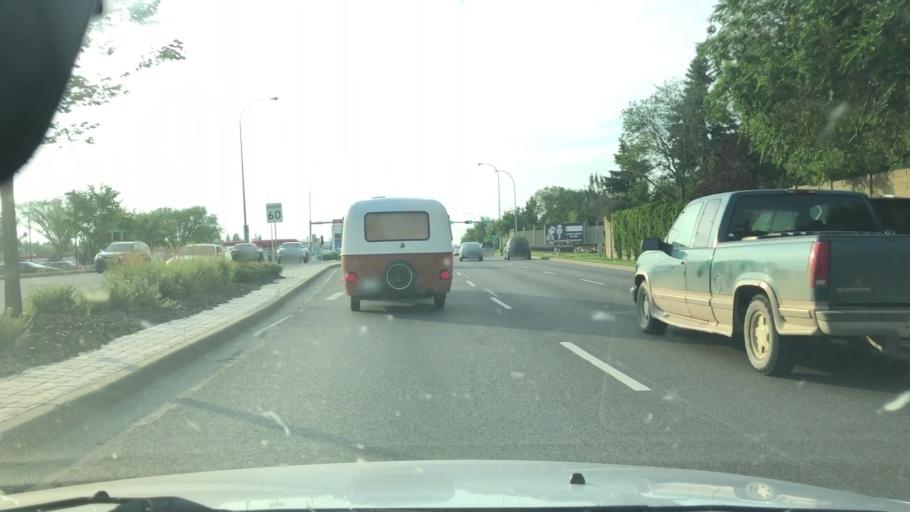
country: CA
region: Alberta
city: St. Albert
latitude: 53.6226
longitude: -113.6117
